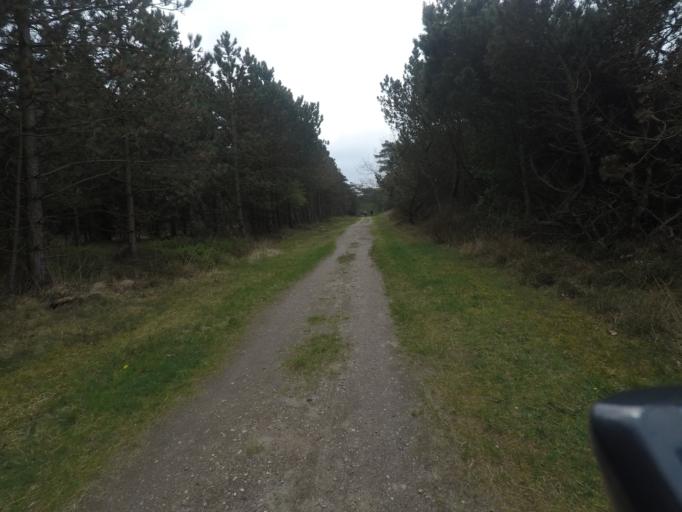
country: DE
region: Schleswig-Holstein
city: List
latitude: 55.0976
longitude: 8.5244
